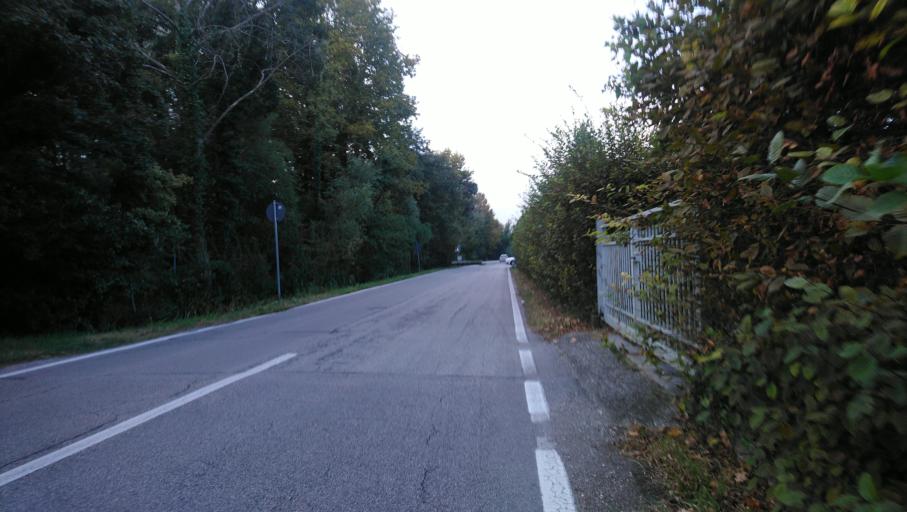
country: IT
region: Veneto
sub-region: Provincia di Treviso
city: Treviso
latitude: 45.6877
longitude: 12.2427
